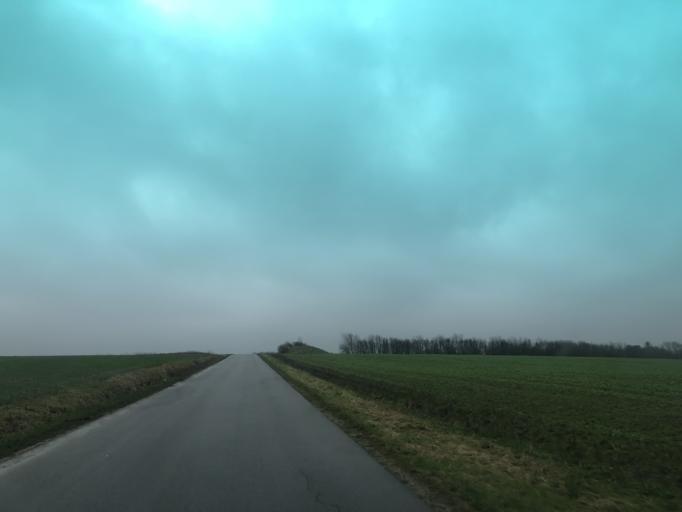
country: DK
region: Central Jutland
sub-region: Struer Kommune
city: Struer
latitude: 56.4458
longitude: 8.5879
